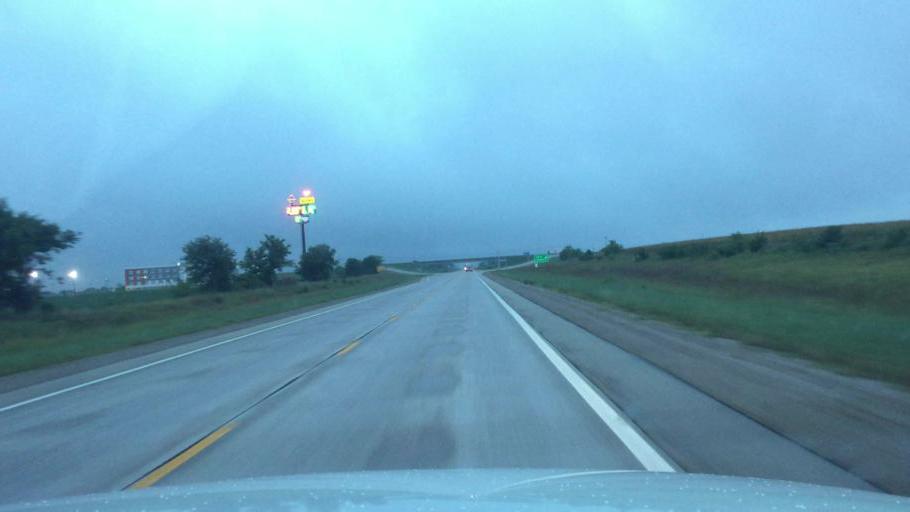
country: US
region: Kansas
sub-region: Neosho County
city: Chanute
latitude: 37.6513
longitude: -95.4797
